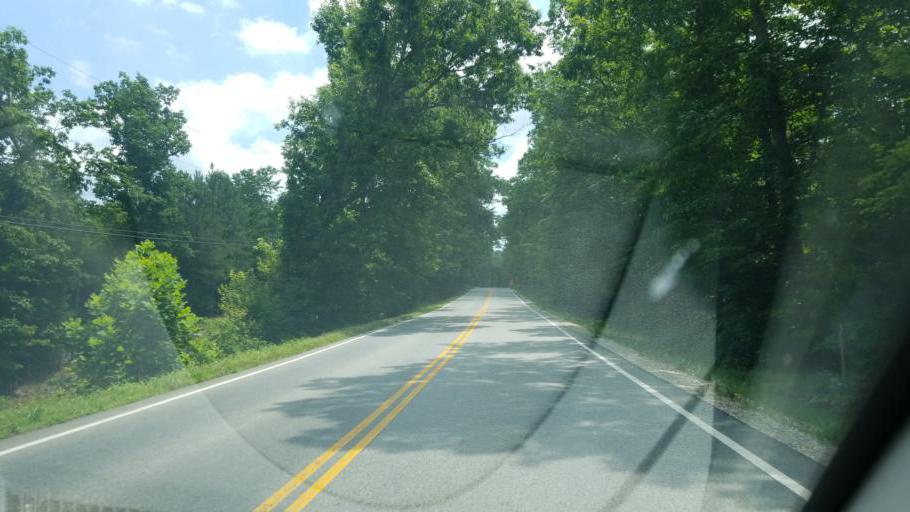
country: US
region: Virginia
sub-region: Nelson County
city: Lovingston
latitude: 37.5618
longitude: -78.8438
